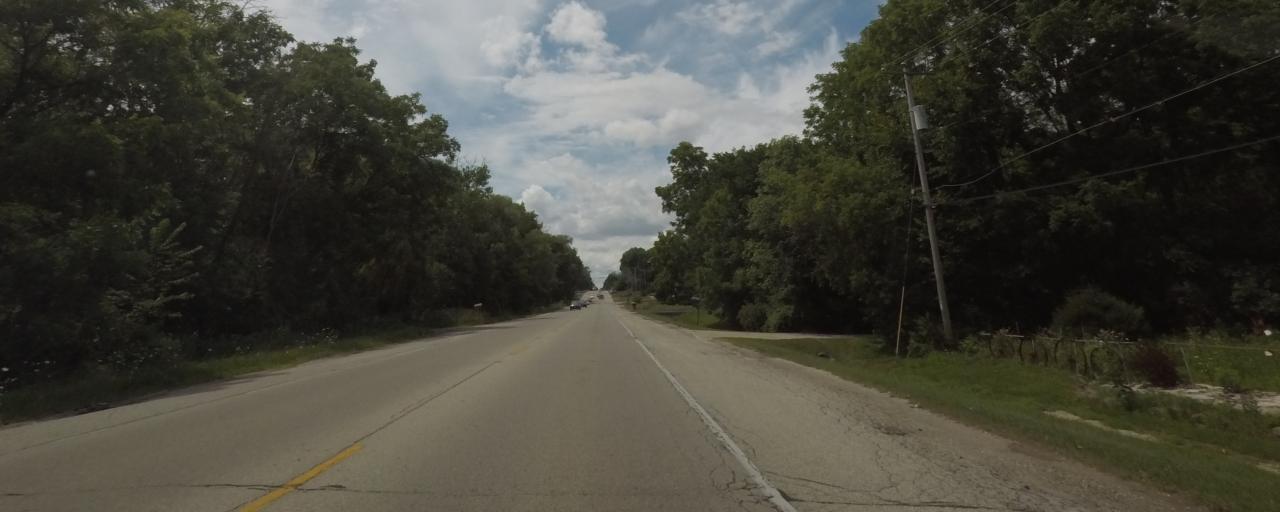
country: US
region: Wisconsin
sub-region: Waukesha County
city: New Berlin
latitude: 42.9956
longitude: -88.0734
